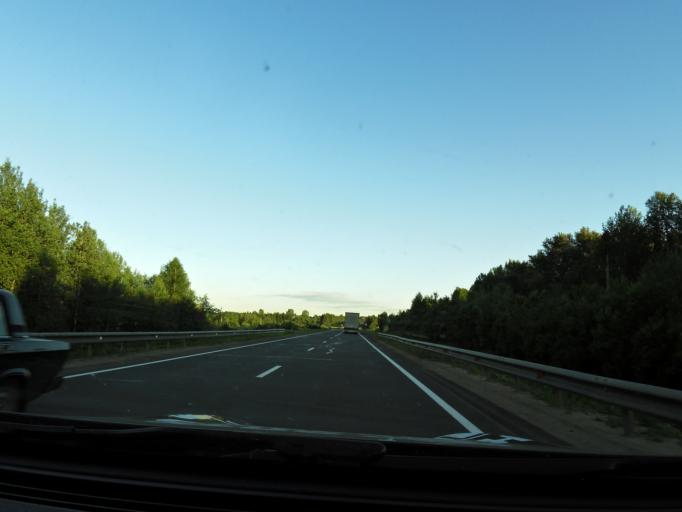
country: RU
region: Vologda
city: Gryazovets
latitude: 58.7318
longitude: 40.2927
